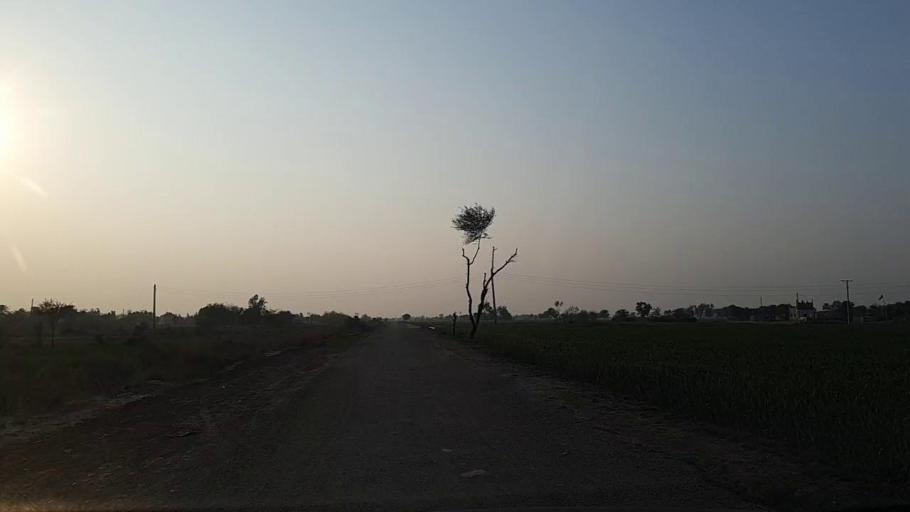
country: PK
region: Sindh
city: Daur
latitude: 26.4164
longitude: 68.3819
